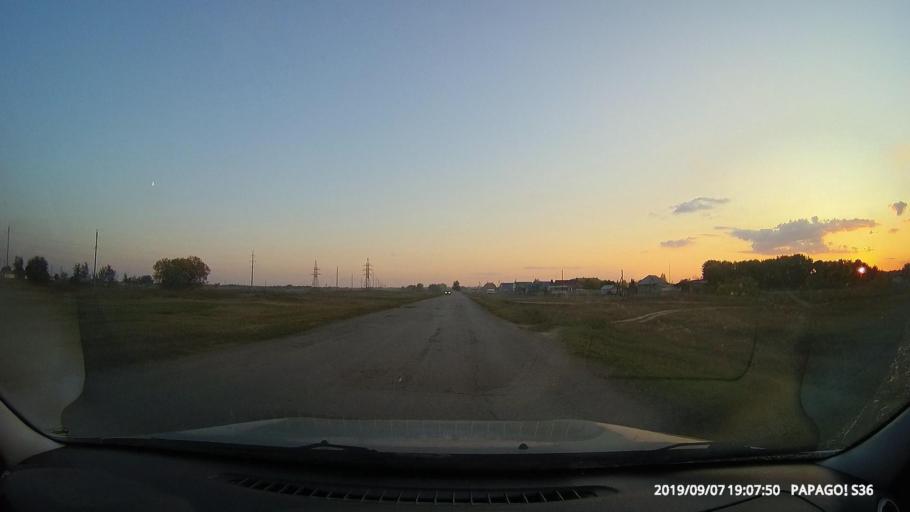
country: RU
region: Samara
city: Chapayevsk
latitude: 52.9944
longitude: 49.7767
